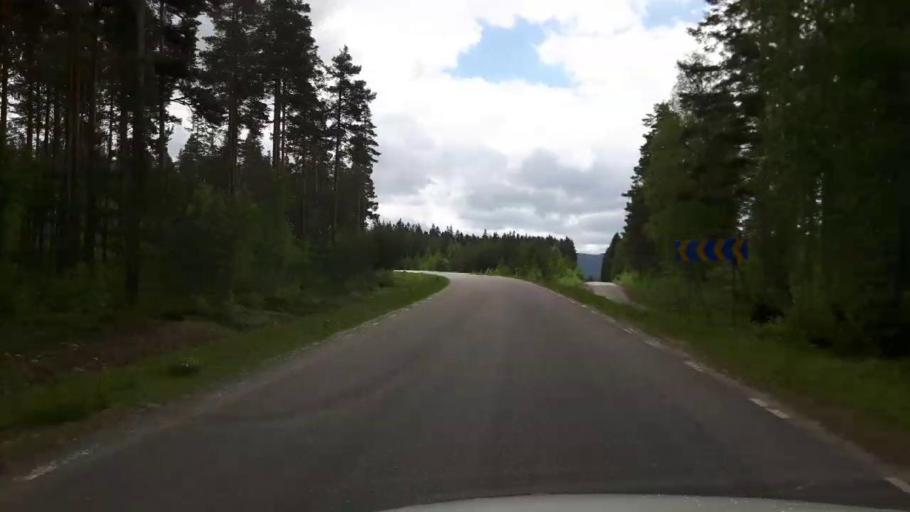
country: SE
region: Gaevleborg
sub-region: Ovanakers Kommun
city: Alfta
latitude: 61.3246
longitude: 15.9738
